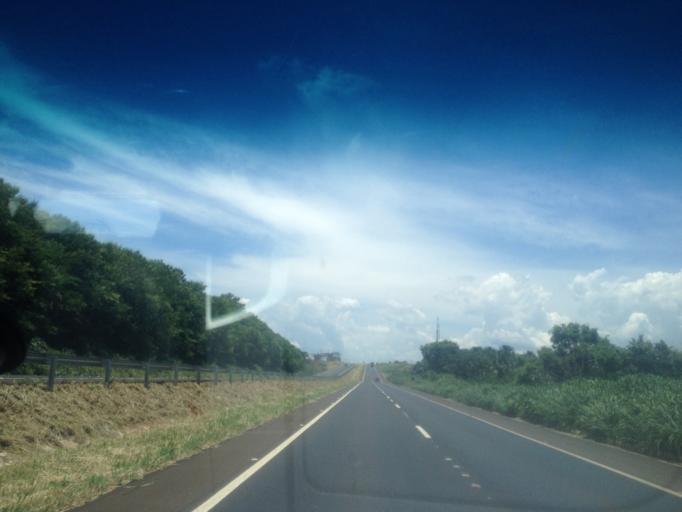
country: BR
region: Minas Gerais
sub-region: Uberlandia
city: Uberlandia
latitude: -18.8952
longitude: -48.4003
